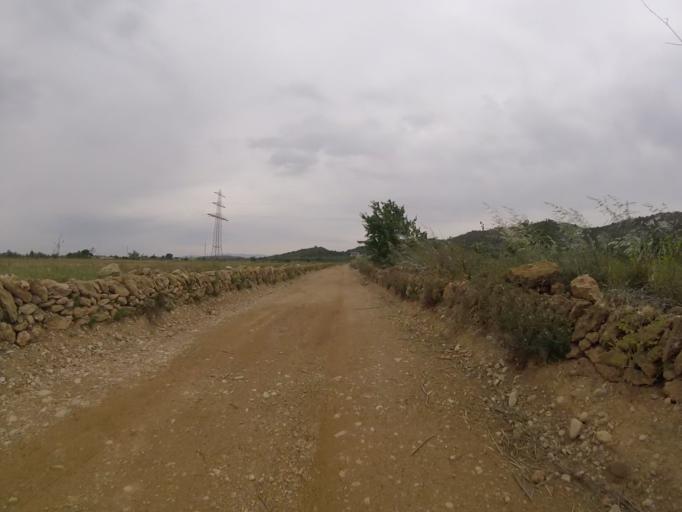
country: ES
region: Valencia
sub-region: Provincia de Castello
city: Alcoceber
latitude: 40.2436
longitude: 0.2610
